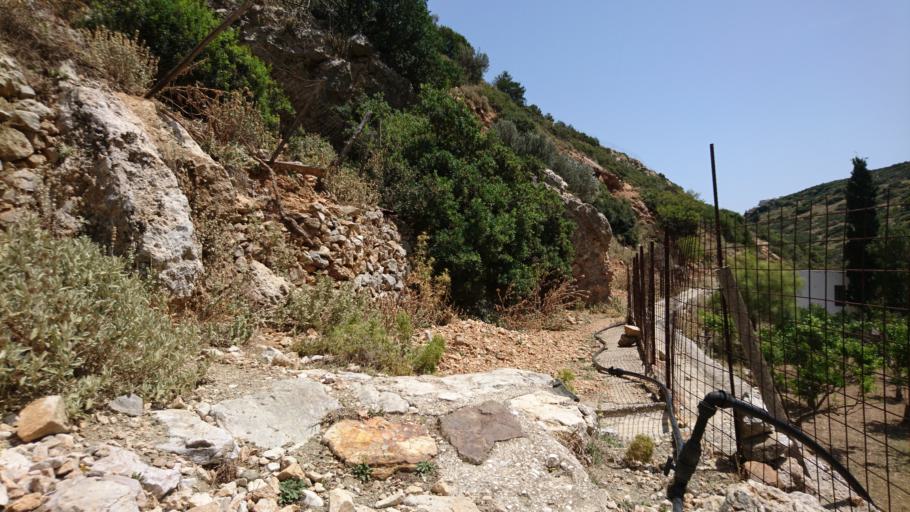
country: GR
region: Central Greece
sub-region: Nomos Evvoias
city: Skyros
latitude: 38.9052
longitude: 24.5517
